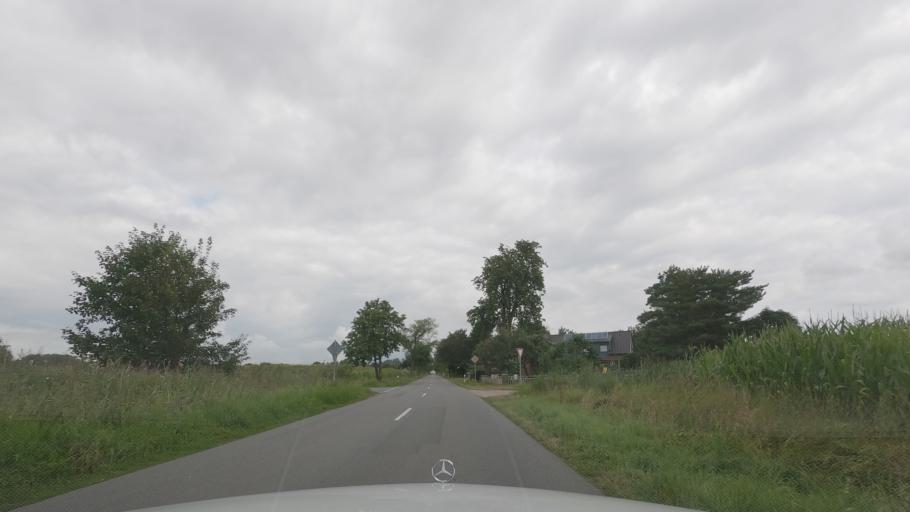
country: DE
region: Lower Saxony
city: Neuenkirchen
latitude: 53.2897
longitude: 8.5315
